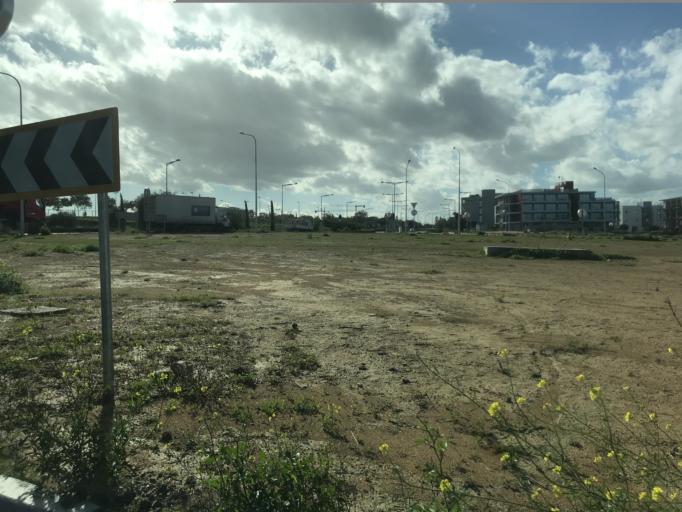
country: CY
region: Lefkosia
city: Geri
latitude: 35.1497
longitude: 33.4111
